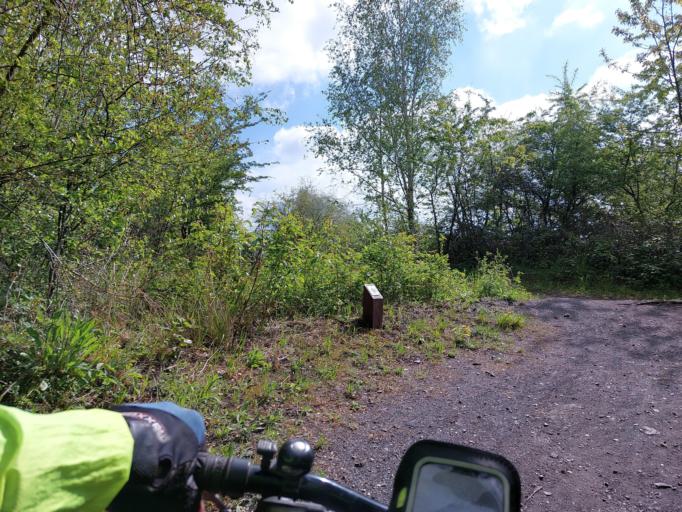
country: BE
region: Wallonia
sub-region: Province du Hainaut
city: Colfontaine
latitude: 50.4205
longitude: 3.8680
